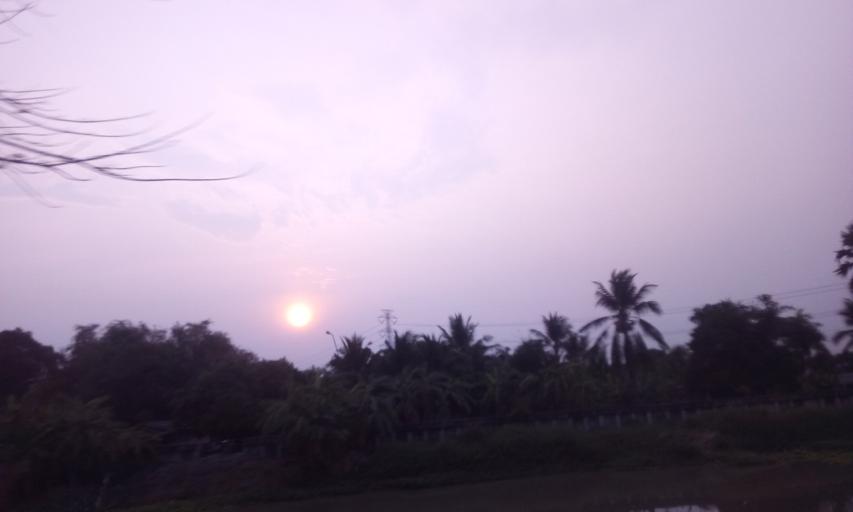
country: TH
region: Bangkok
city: Nong Chok
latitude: 13.9272
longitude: 100.8927
